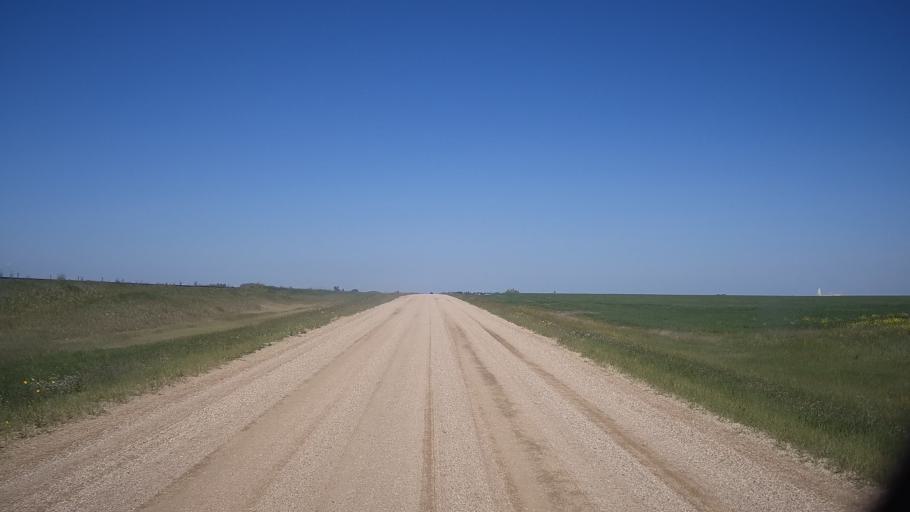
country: CA
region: Saskatchewan
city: Watrous
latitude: 51.8786
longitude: -106.0156
